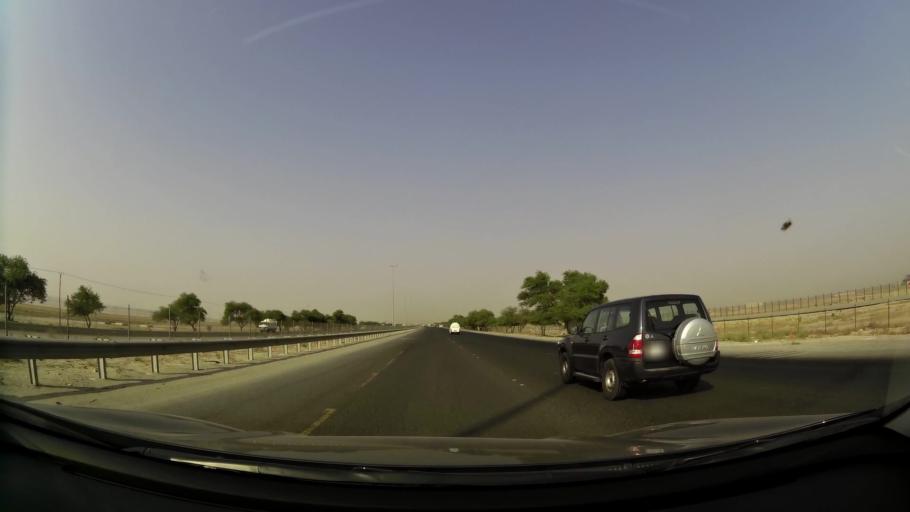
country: KW
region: Al Farwaniyah
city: Janub as Surrah
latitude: 29.1813
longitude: 47.9790
